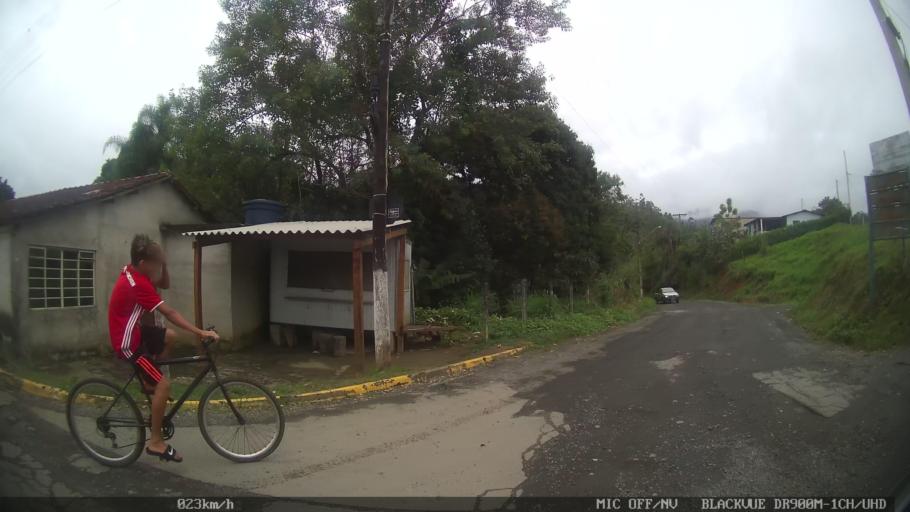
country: BR
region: Sao Paulo
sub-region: Cajati
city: Cajati
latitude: -24.7887
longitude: -48.1763
